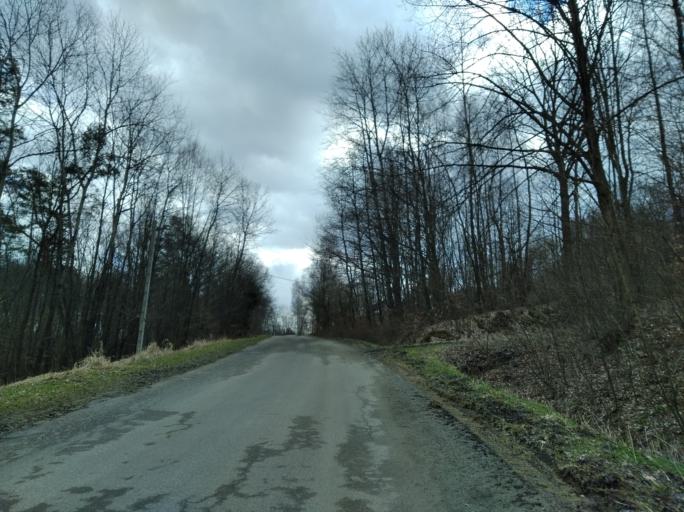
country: PL
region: Subcarpathian Voivodeship
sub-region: Powiat krosnienski
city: Odrzykon
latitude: 49.7843
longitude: 21.7351
